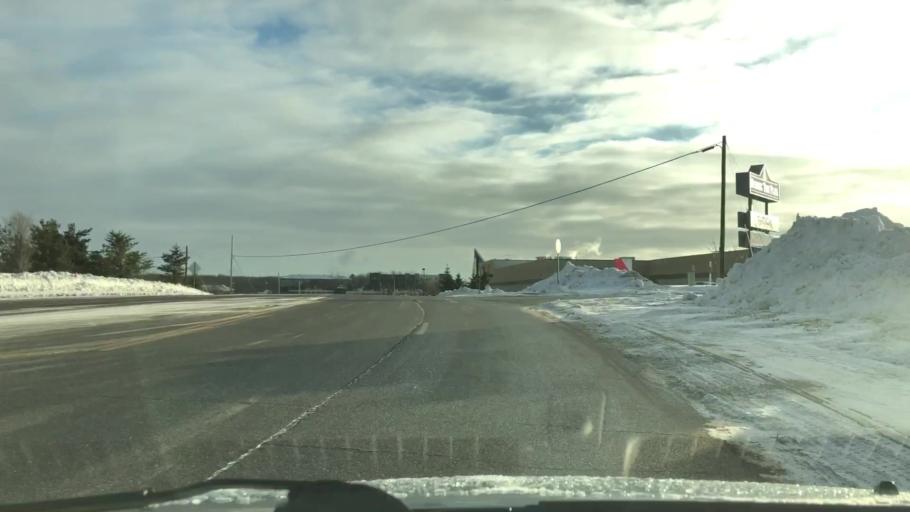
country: US
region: Minnesota
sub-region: Saint Louis County
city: Duluth
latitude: 46.8101
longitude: -92.1693
